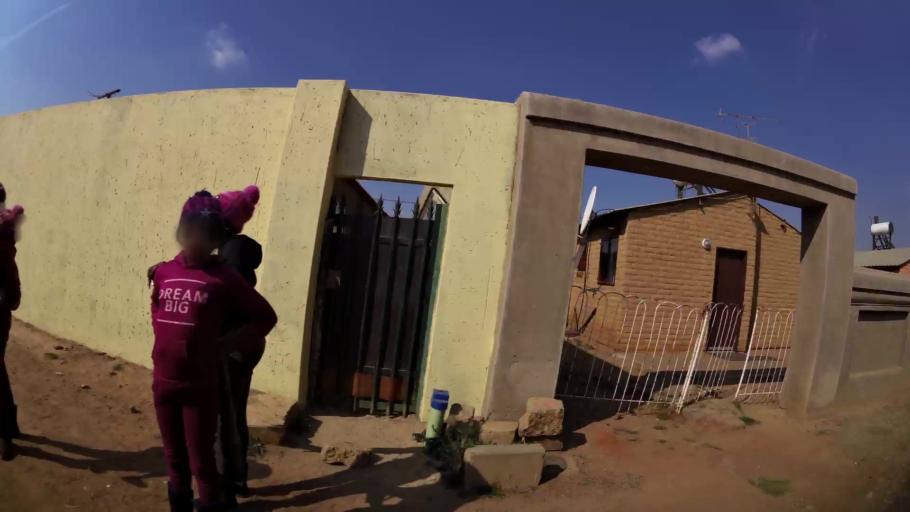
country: ZA
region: Gauteng
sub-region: Ekurhuleni Metropolitan Municipality
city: Springs
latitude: -26.1120
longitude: 28.4809
